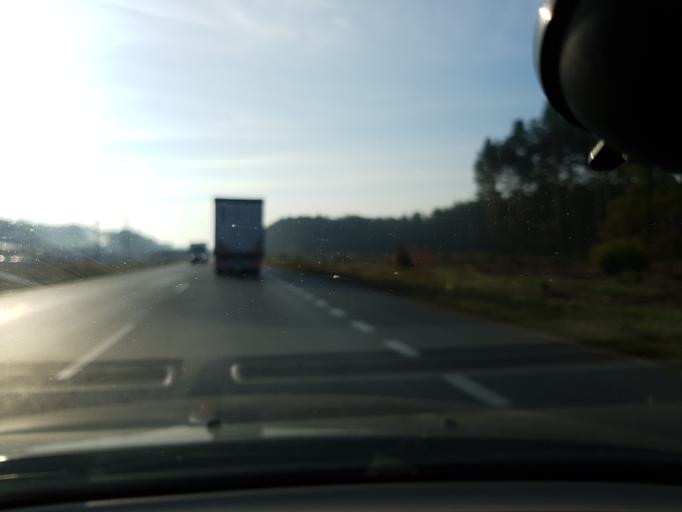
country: PL
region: Masovian Voivodeship
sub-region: Powiat otwocki
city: Otwock
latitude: 52.1588
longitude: 21.3064
